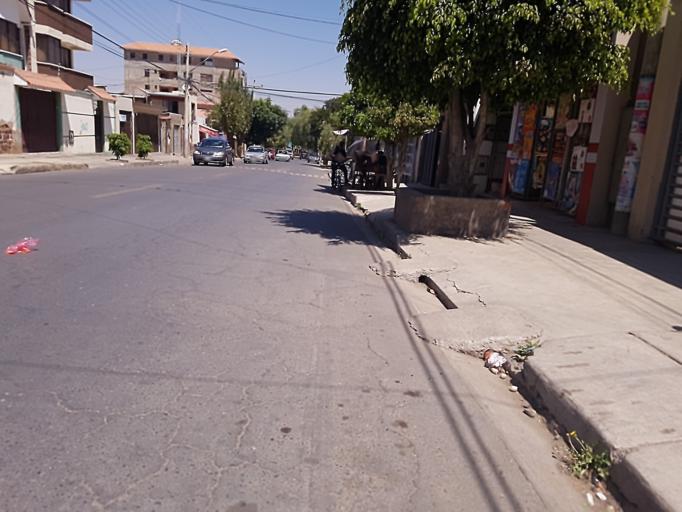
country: BO
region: Cochabamba
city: Cochabamba
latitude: -17.3610
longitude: -66.1847
